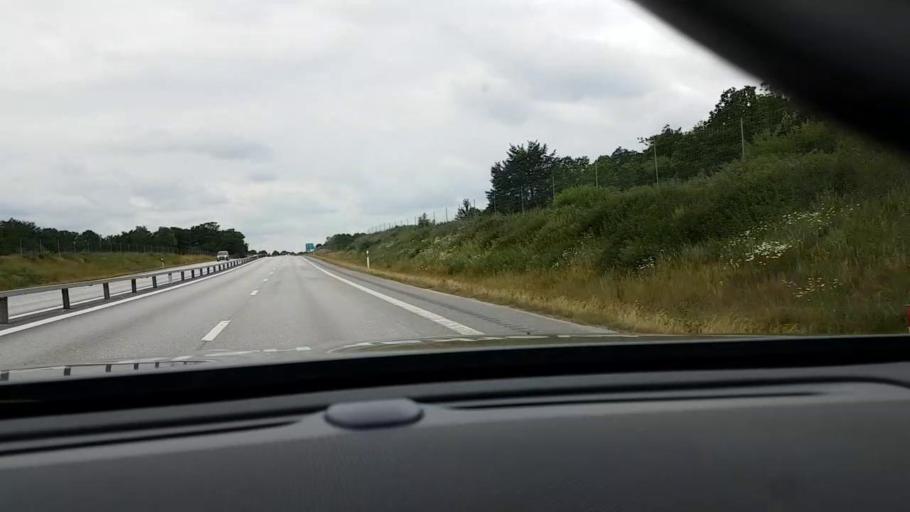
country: SE
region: Skane
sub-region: Horby Kommun
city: Hoerby
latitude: 55.8737
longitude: 13.7069
